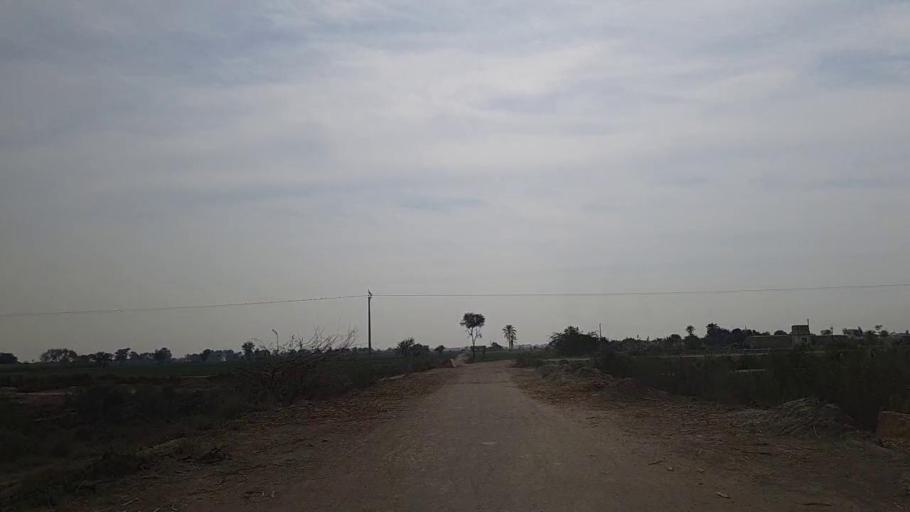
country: PK
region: Sindh
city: Daur
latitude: 26.4520
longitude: 68.4352
